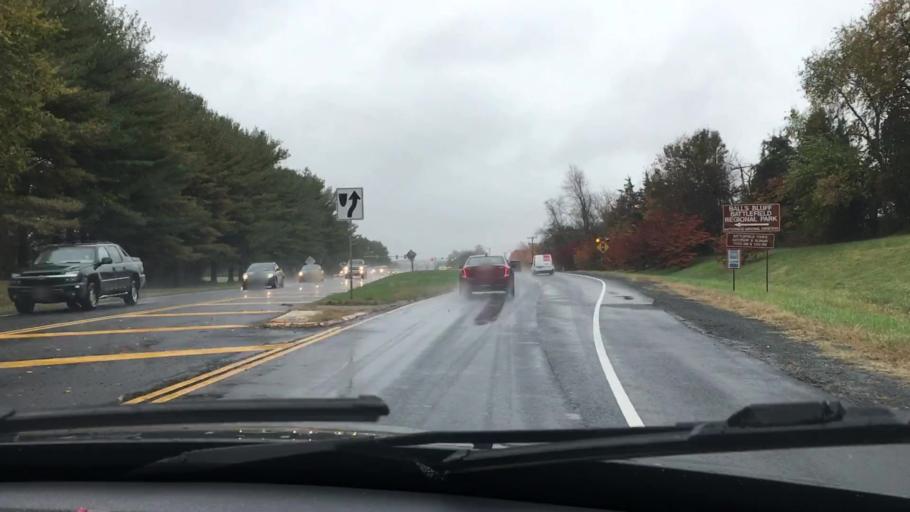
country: US
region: Virginia
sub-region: Loudoun County
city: Leesburg
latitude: 39.1286
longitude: -77.5439
